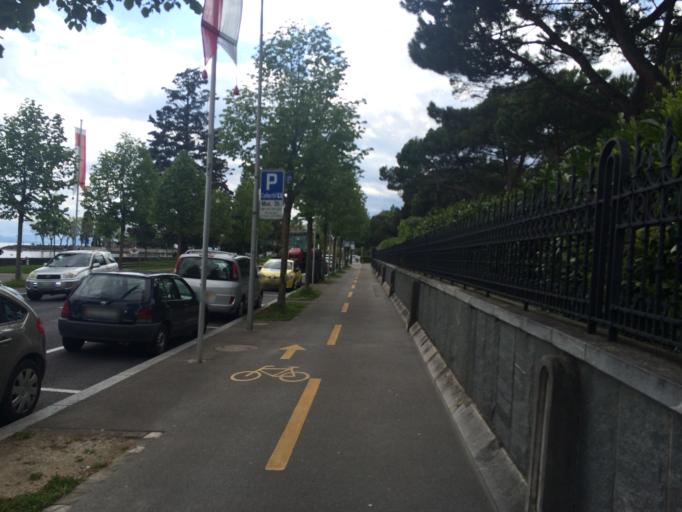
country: CH
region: Vaud
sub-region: Lausanne District
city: Lausanne
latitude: 46.5074
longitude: 6.6315
